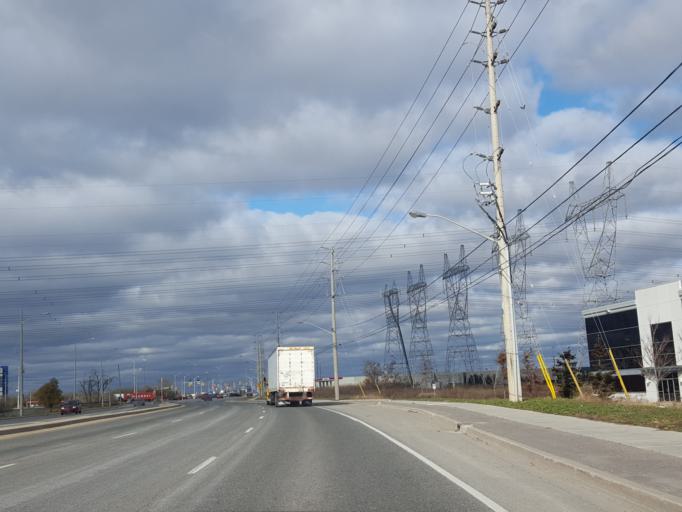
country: CA
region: Ontario
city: Brampton
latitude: 43.7210
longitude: -79.6652
